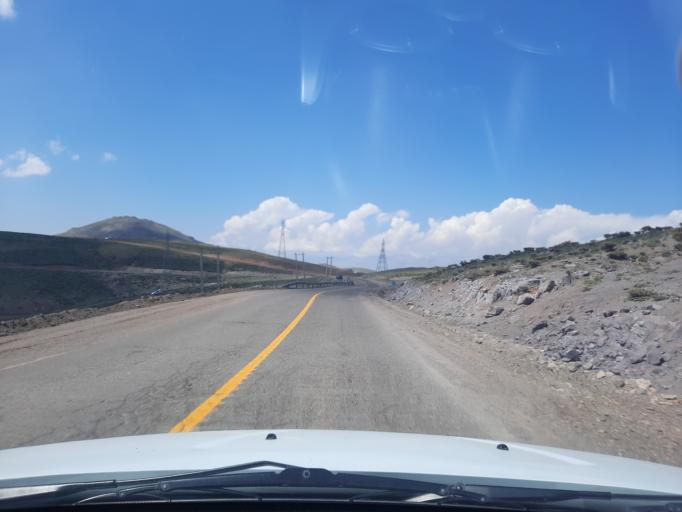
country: IR
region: Qazvin
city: Qazvin
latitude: 36.3910
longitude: 50.2080
